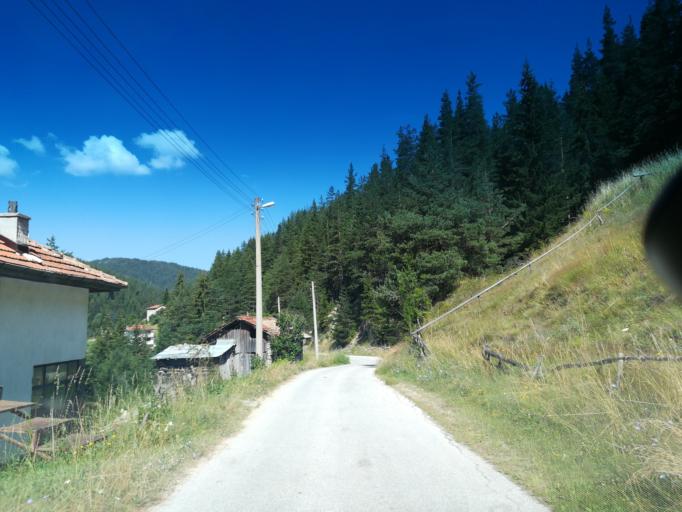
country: BG
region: Smolyan
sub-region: Obshtina Smolyan
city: Smolyan
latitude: 41.6575
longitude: 24.8241
